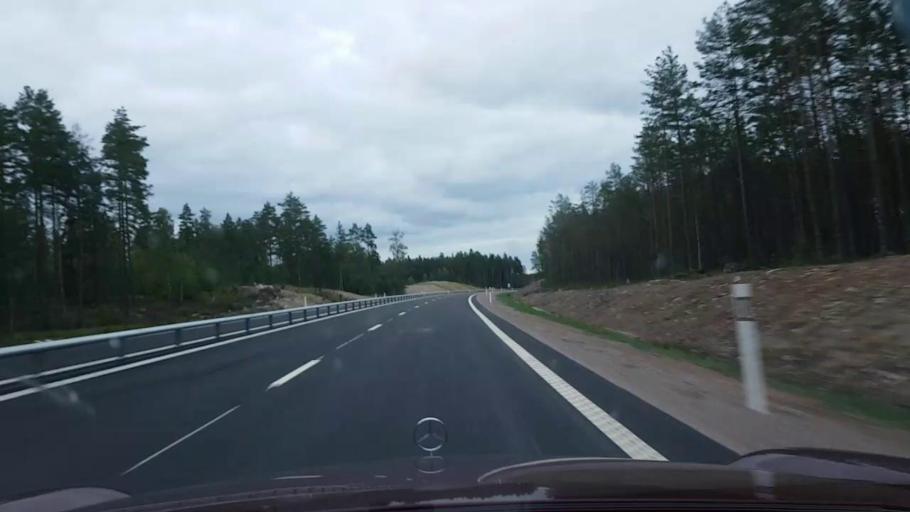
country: SE
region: Vaestmanland
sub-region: Surahammars Kommun
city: Surahammar
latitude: 59.6806
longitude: 16.2363
